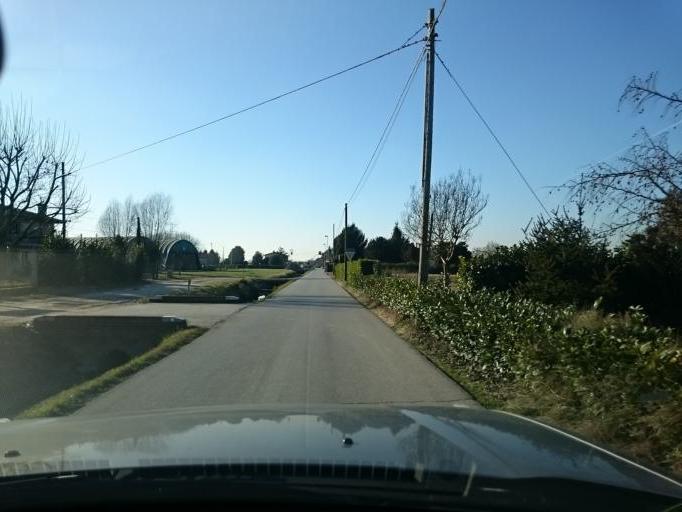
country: IT
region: Veneto
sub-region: Provincia di Venezia
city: Mira Taglio
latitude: 45.4335
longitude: 12.1594
